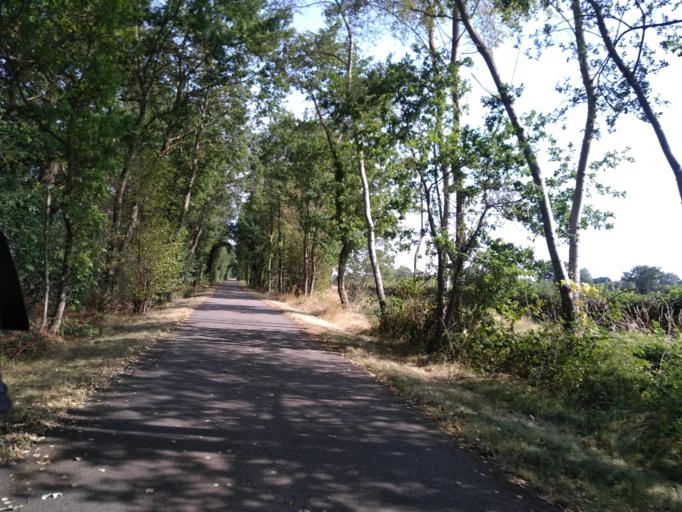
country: FR
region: Bourgogne
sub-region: Departement de Saone-et-Loire
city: Marcigny
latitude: 46.3184
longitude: 4.0285
